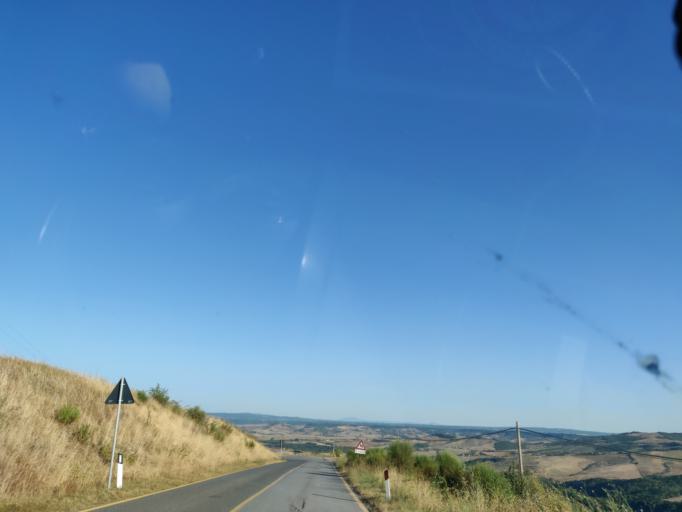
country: IT
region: Tuscany
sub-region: Provincia di Siena
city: Piancastagnaio
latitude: 42.8399
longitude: 11.7061
